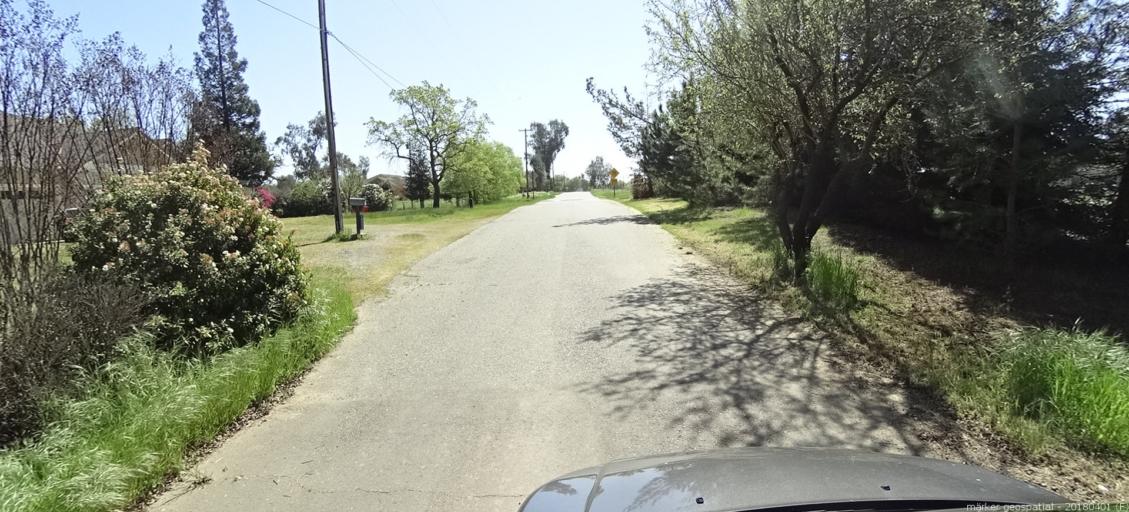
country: US
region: California
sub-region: Sacramento County
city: Wilton
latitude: 38.4146
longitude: -121.2758
